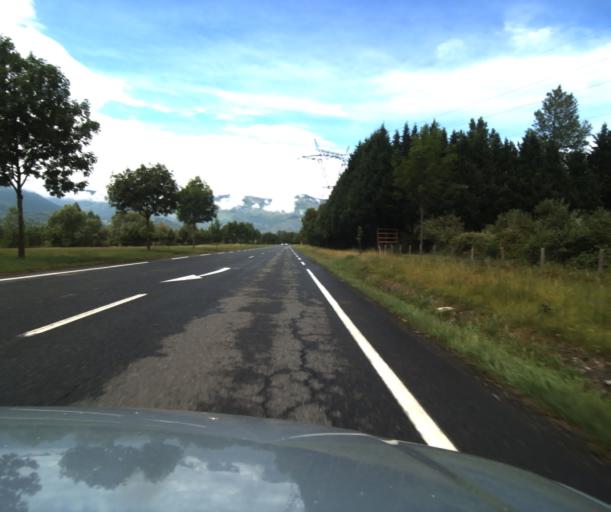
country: FR
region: Midi-Pyrenees
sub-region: Departement des Hautes-Pyrenees
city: Pierrefitte-Nestalas
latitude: 42.9819
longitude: -0.0705
